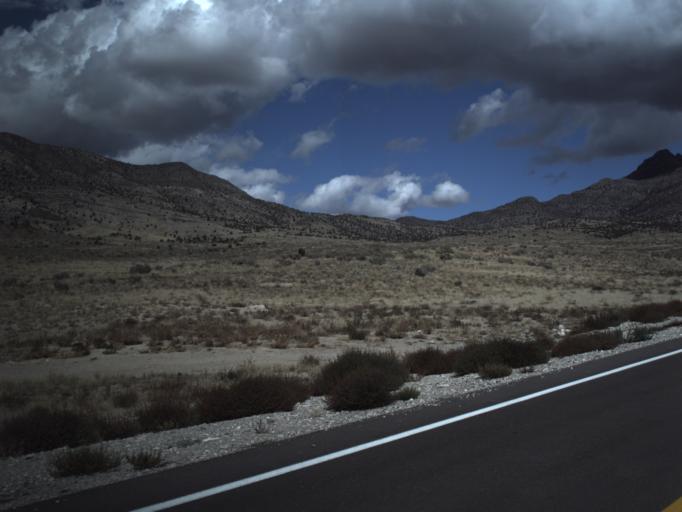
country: US
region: Utah
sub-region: Beaver County
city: Milford
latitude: 38.5104
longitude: -113.5862
